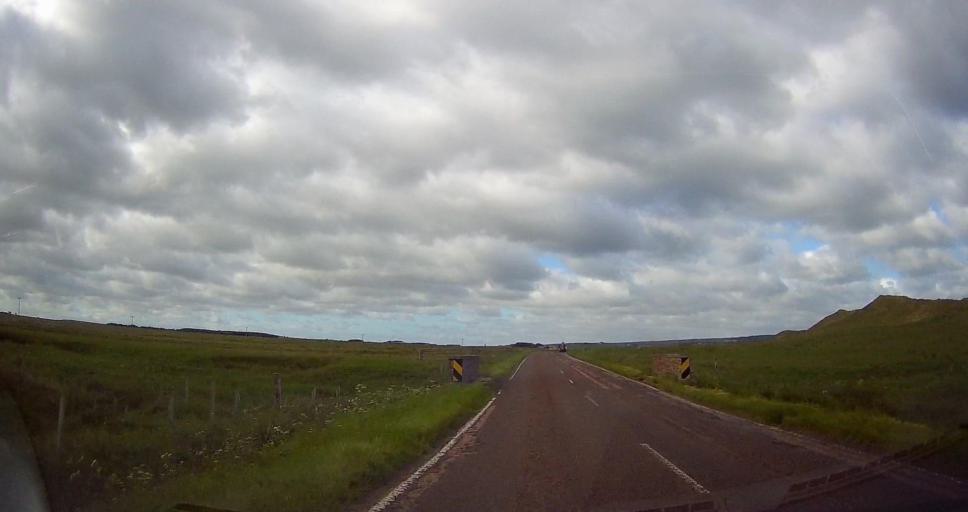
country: GB
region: Scotland
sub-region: Highland
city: Thurso
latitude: 58.6009
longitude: -3.3505
